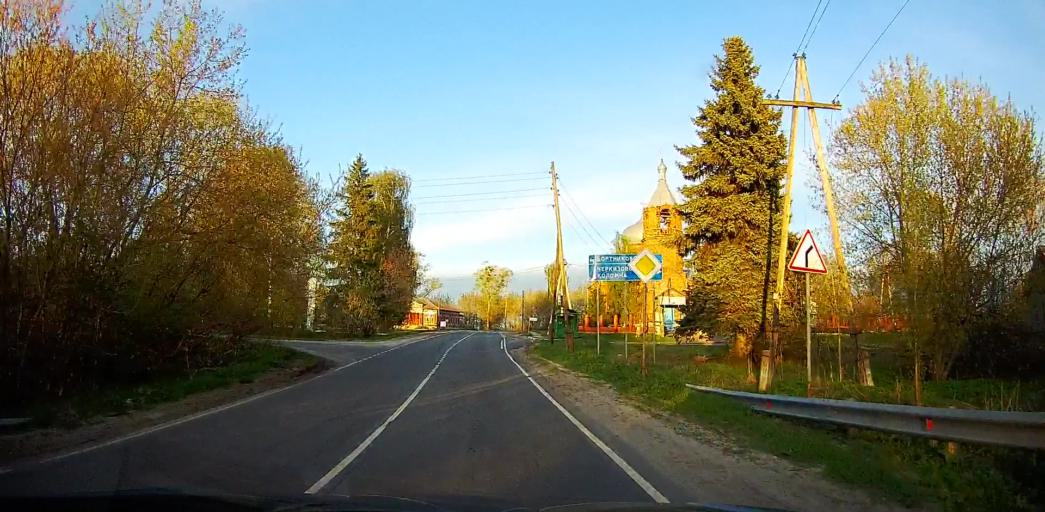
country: RU
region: Moskovskaya
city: Peski
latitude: 55.2151
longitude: 38.6703
